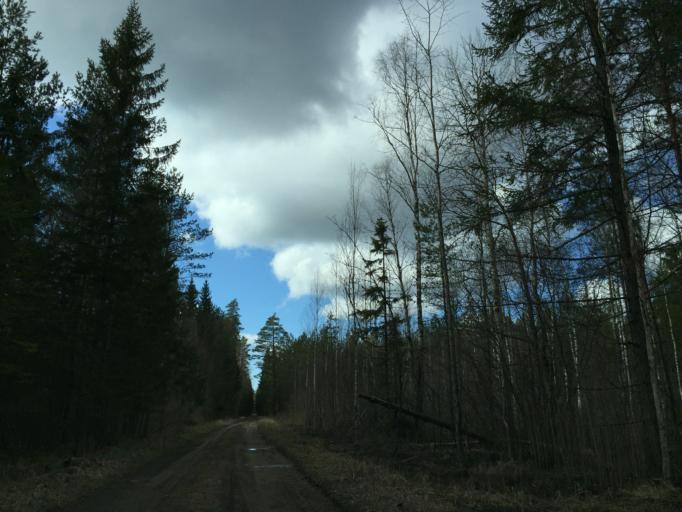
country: LV
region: Garkalne
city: Garkalne
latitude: 56.9482
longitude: 24.4794
